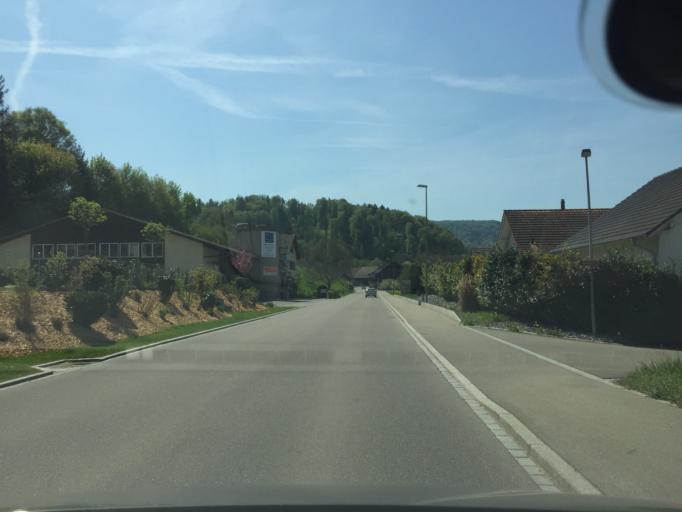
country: CH
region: Zurich
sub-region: Bezirk Buelach
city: Freienstein
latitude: 47.5784
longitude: 8.6109
